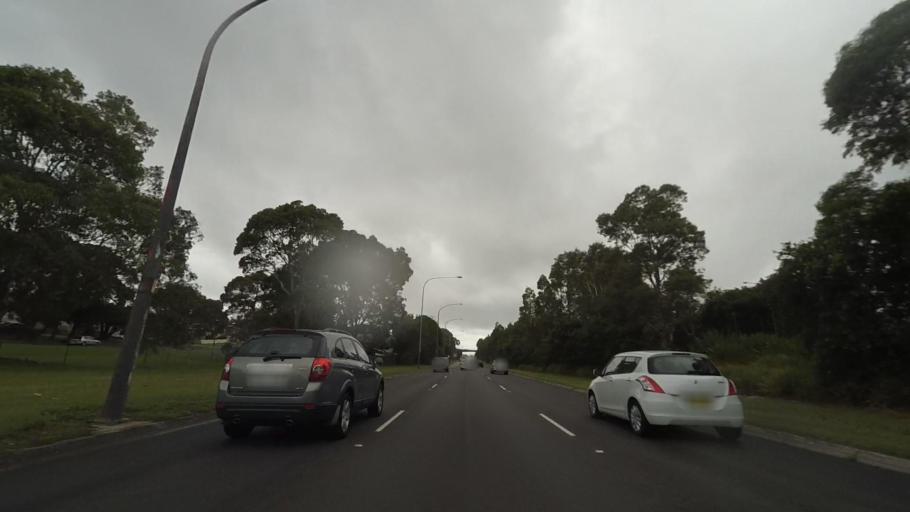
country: AU
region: New South Wales
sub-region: Kogarah
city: Blakehurst
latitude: -34.0159
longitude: 151.1231
